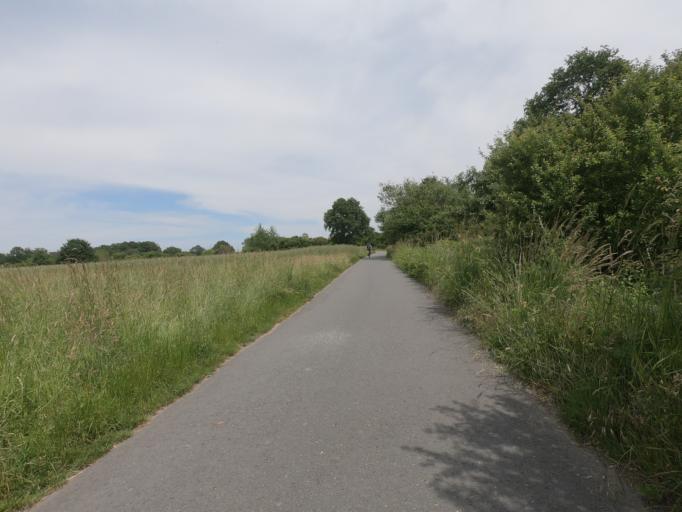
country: DE
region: Hesse
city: Langen
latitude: 50.0039
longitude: 8.6639
